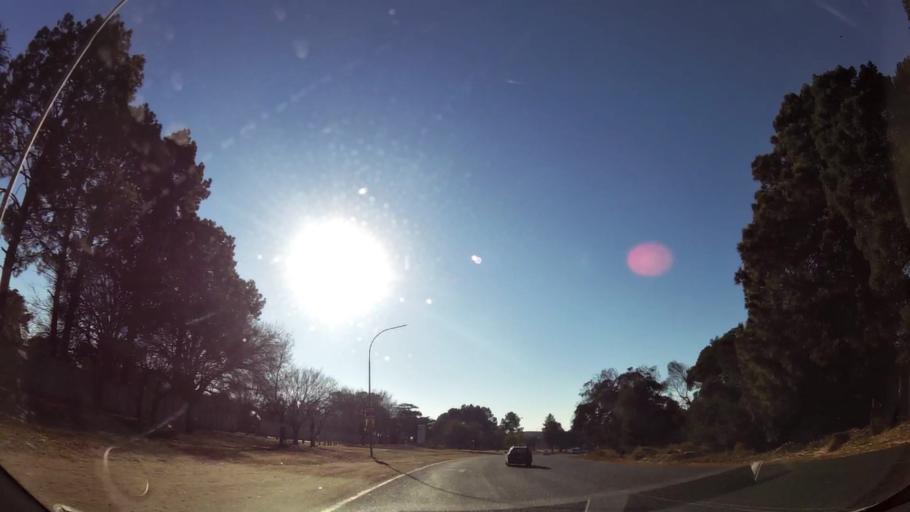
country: ZA
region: Gauteng
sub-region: Ekurhuleni Metropolitan Municipality
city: Tembisa
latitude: -26.0396
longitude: 28.2499
